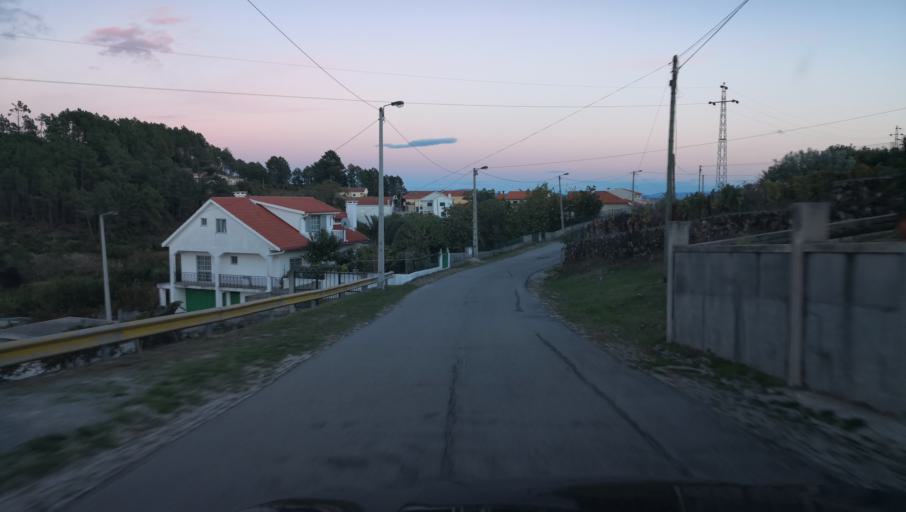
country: PT
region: Vila Real
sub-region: Santa Marta de Penaguiao
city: Santa Marta de Penaguiao
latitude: 41.2633
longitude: -7.7909
